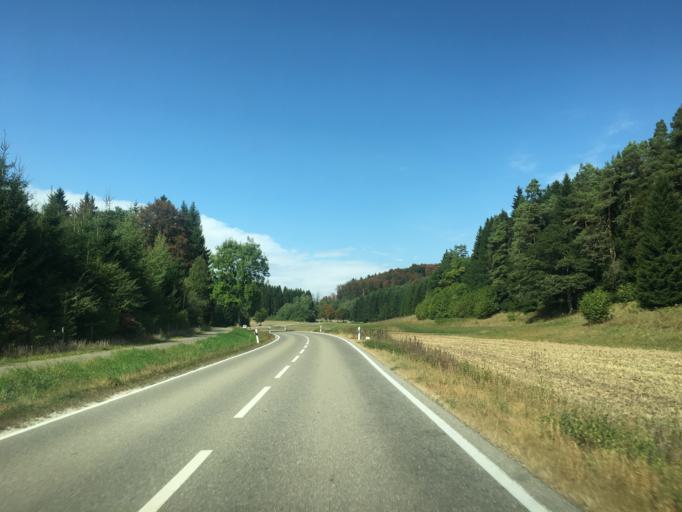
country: DE
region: Baden-Wuerttemberg
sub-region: Tuebingen Region
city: Trochtelfingen
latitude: 48.3701
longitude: 9.1994
